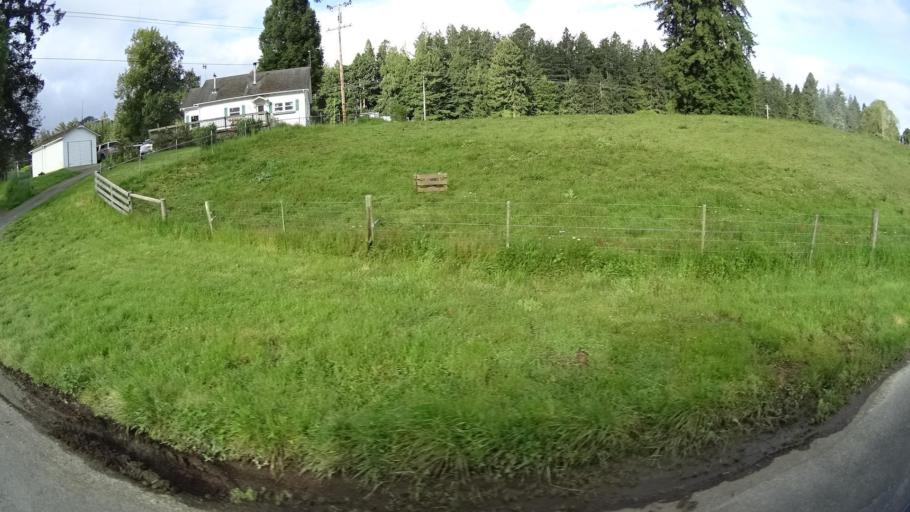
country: US
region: California
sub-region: Humboldt County
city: Blue Lake
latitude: 40.8721
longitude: -124.0050
